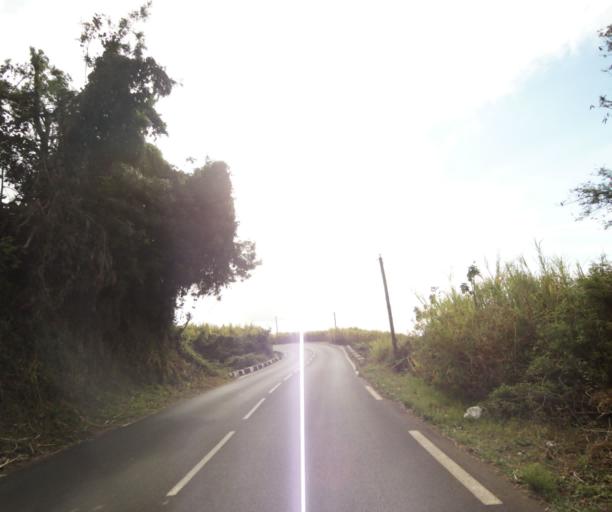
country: RE
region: Reunion
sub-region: Reunion
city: Saint-Paul
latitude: -21.0259
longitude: 55.3139
